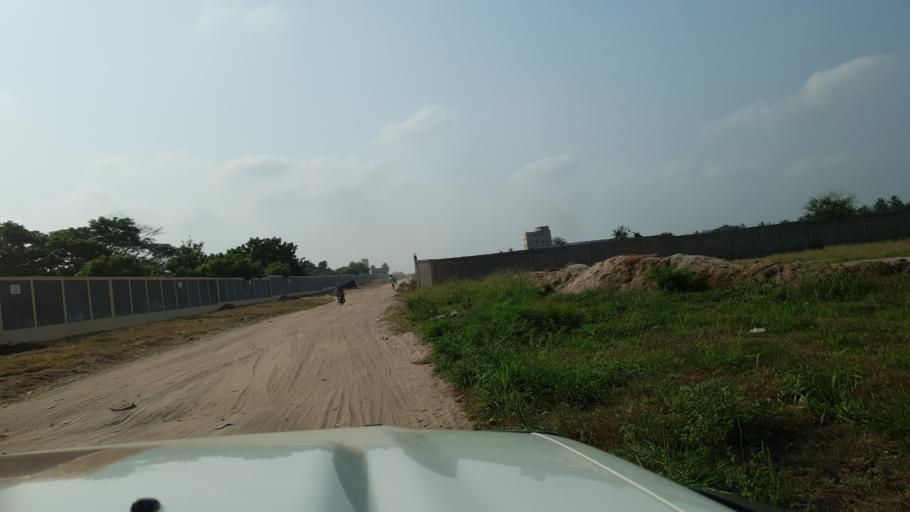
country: TG
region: Maritime
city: Lome
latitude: 6.1743
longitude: 1.2096
